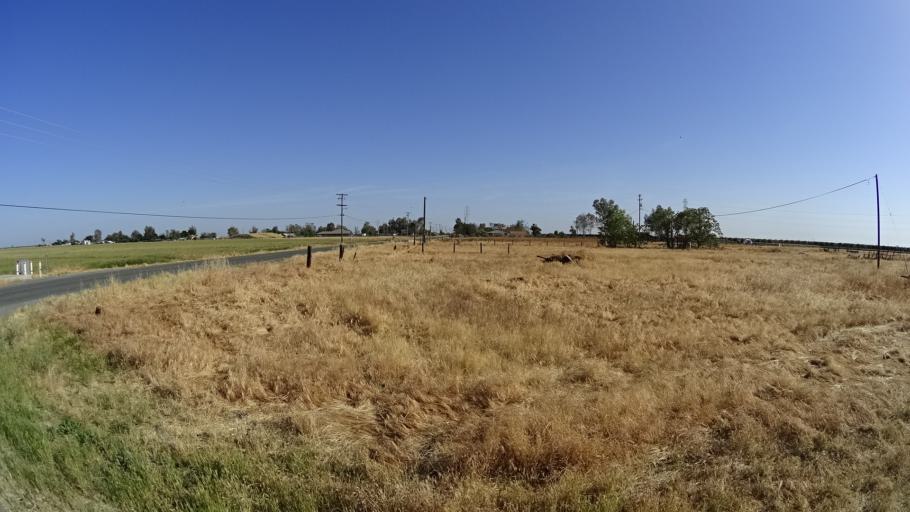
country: US
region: California
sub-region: Kings County
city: Corcoran
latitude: 36.1162
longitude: -119.5631
